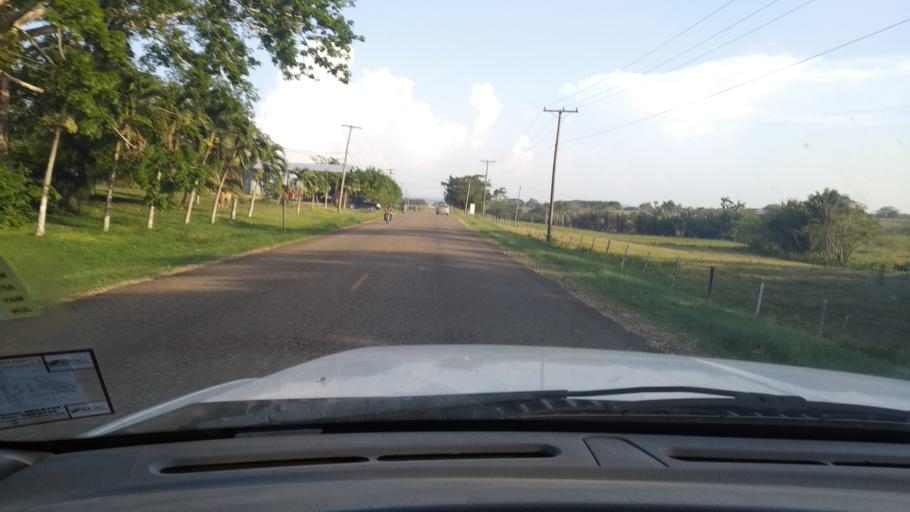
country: BZ
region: Cayo
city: San Ignacio
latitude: 17.2549
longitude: -88.9873
